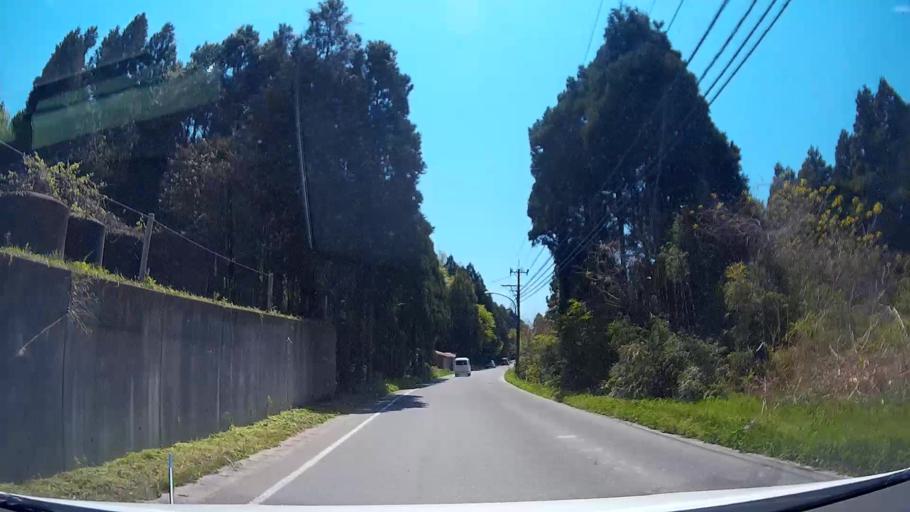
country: JP
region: Ishikawa
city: Nanao
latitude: 37.4541
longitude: 137.3013
